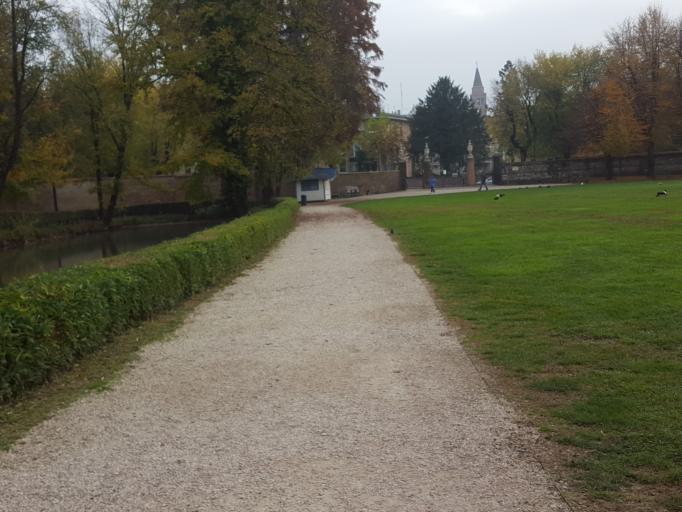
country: IT
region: Veneto
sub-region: Provincia di Vicenza
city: Vicenza
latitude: 45.5535
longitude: 11.5481
